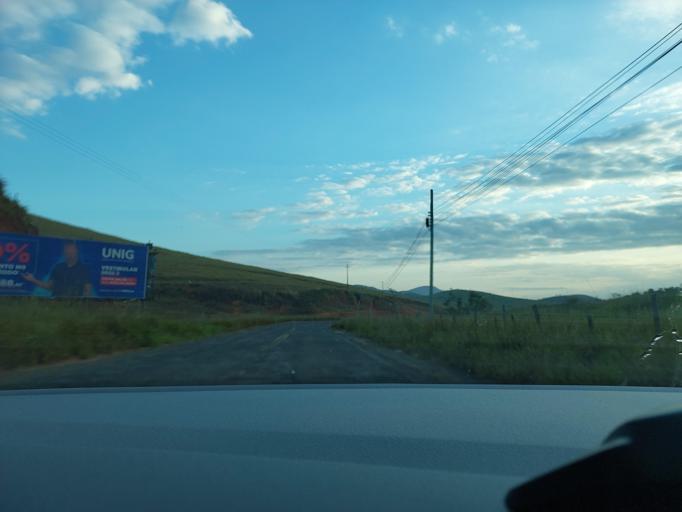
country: BR
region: Rio de Janeiro
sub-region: Natividade
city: Natividade
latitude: -21.1916
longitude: -42.1124
